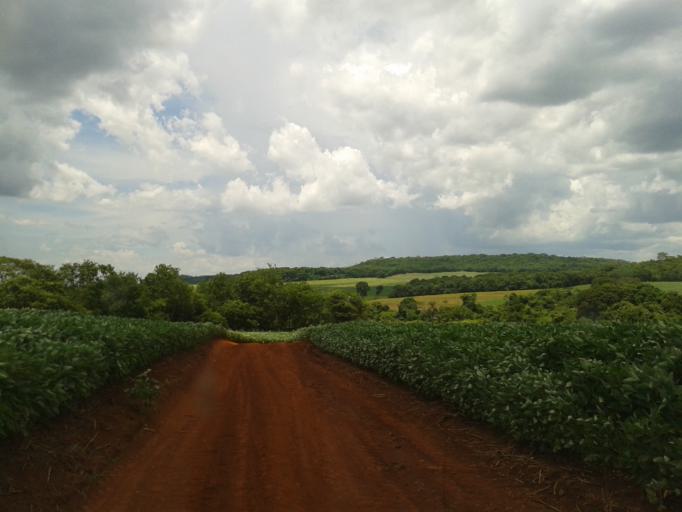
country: BR
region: Minas Gerais
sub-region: Centralina
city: Centralina
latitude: -18.6832
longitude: -49.2188
